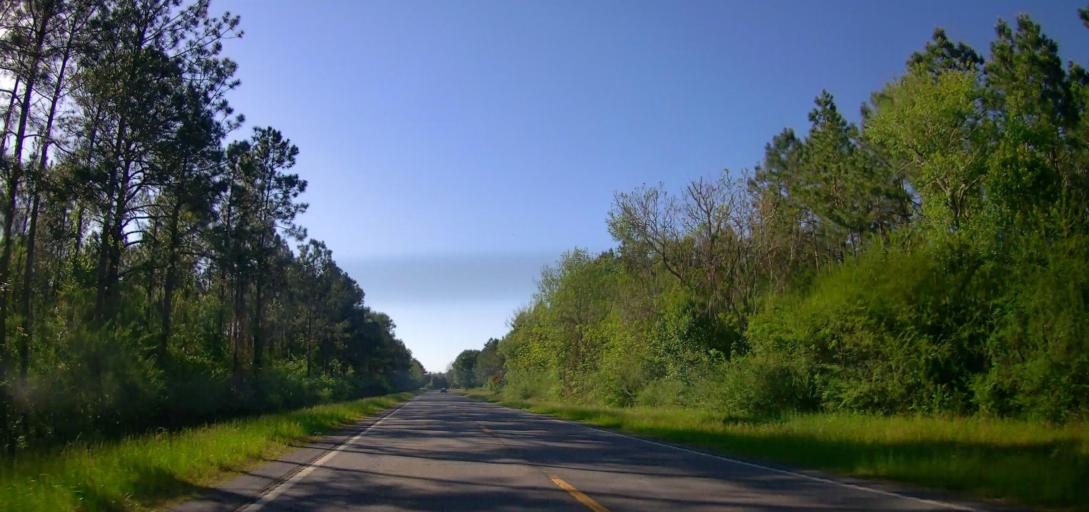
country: US
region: Georgia
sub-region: Ben Hill County
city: Fitzgerald
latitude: 31.7015
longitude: -83.3057
